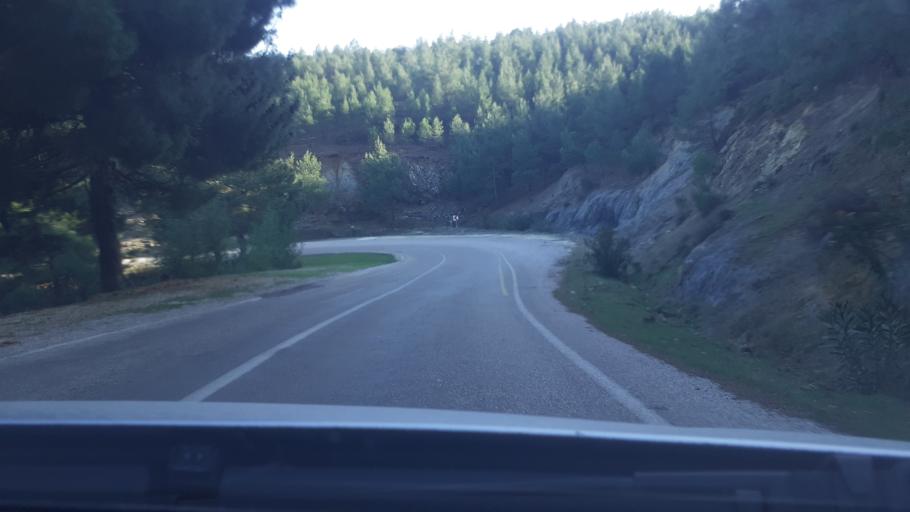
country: TR
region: Hatay
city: Aktepe
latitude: 36.7354
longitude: 36.4654
